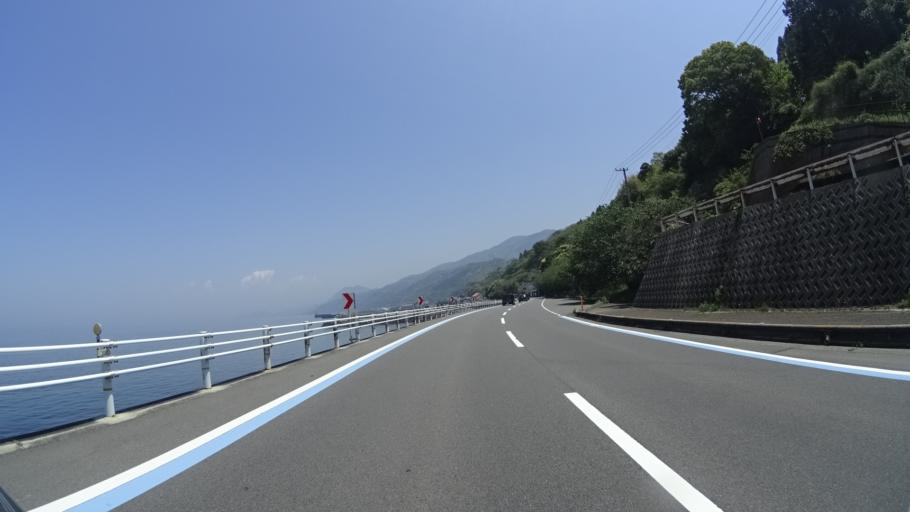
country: JP
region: Ehime
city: Ozu
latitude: 33.6488
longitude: 132.5673
